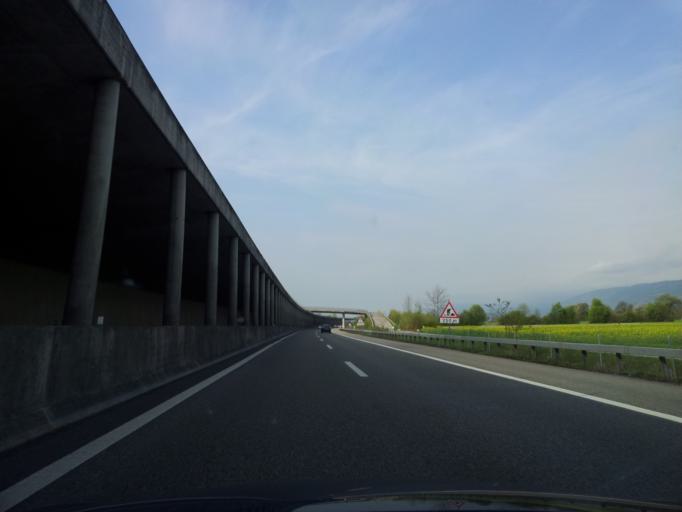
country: CH
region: Bern
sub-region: Seeland District
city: Leuzigen
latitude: 47.1790
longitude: 7.4504
